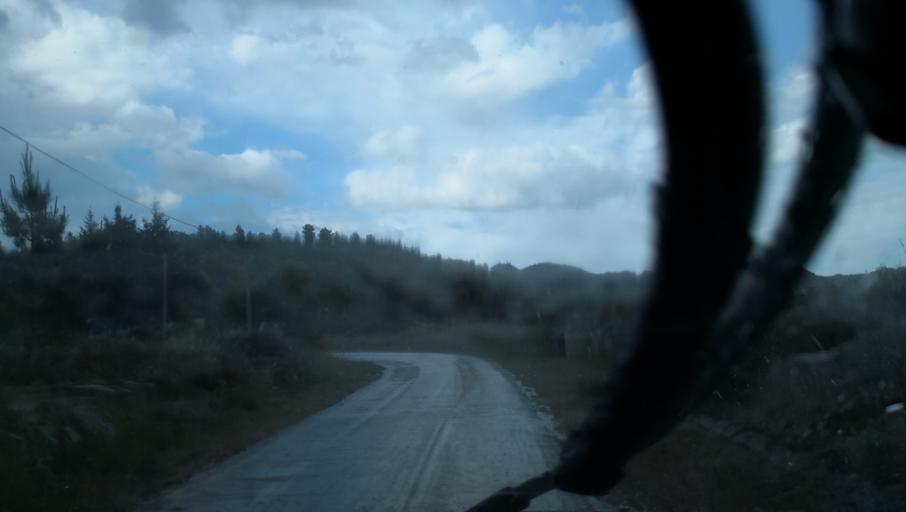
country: PT
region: Vila Real
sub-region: Vila Real
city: Vila Real
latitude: 41.3649
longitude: -7.6971
